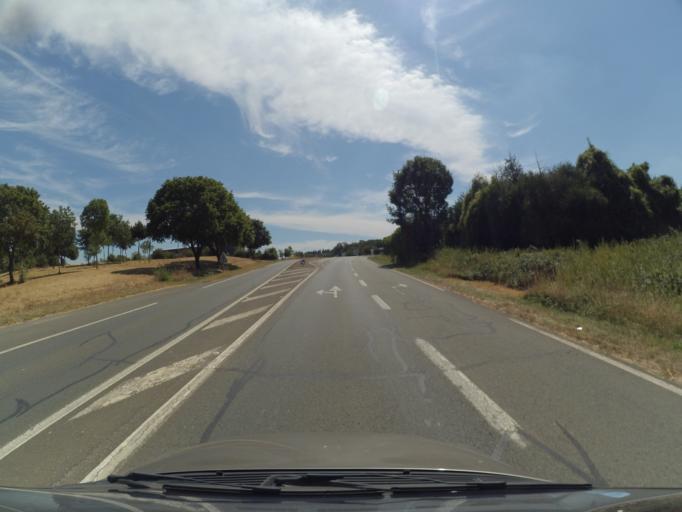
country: FR
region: Poitou-Charentes
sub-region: Departement de la Vienne
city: Lusignan
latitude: 46.4306
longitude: 0.1079
